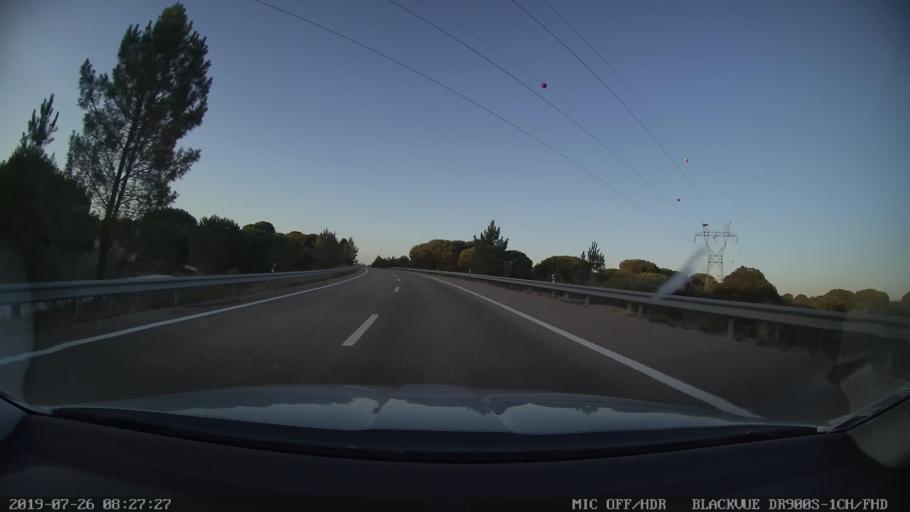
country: PT
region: Evora
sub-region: Vendas Novas
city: Vendas Novas
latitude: 38.6031
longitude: -8.6412
